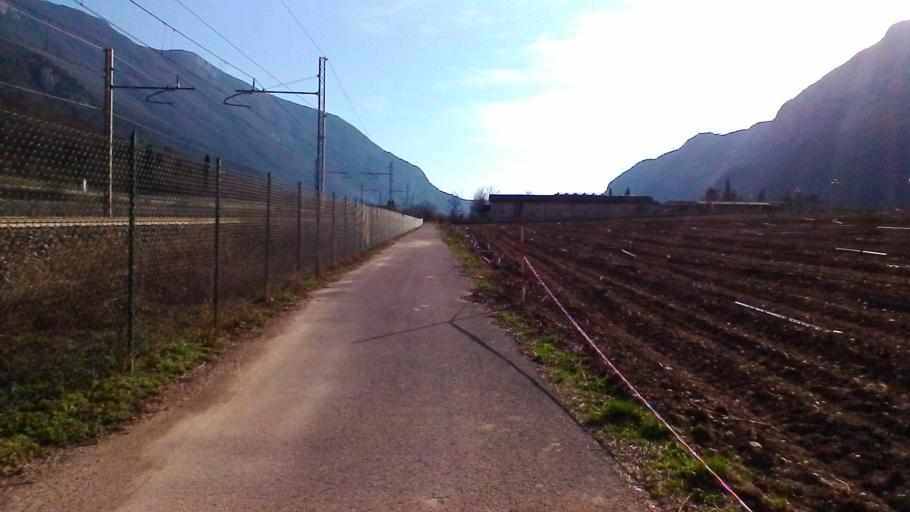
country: IT
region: Veneto
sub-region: Provincia di Verona
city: Dolce
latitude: 45.6130
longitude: 10.8595
